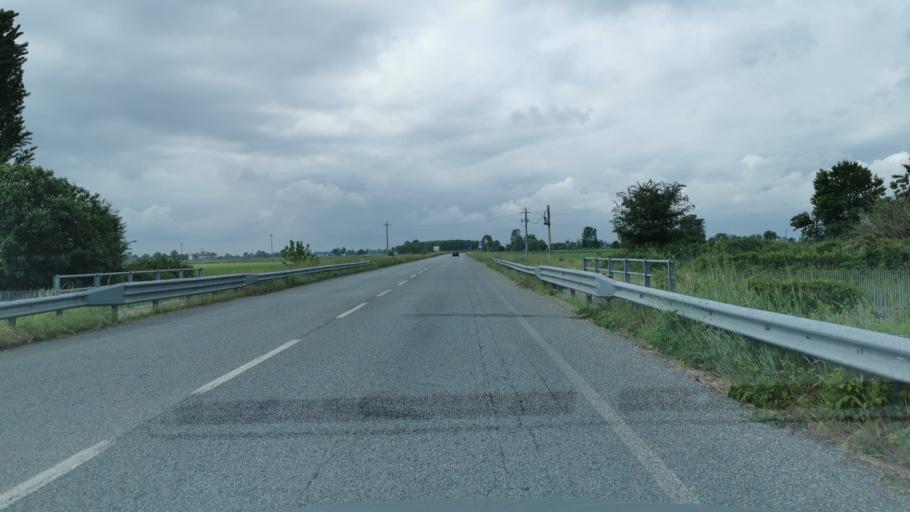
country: IT
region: Piedmont
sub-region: Provincia di Cuneo
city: Racconigi
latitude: 44.7548
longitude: 7.6938
